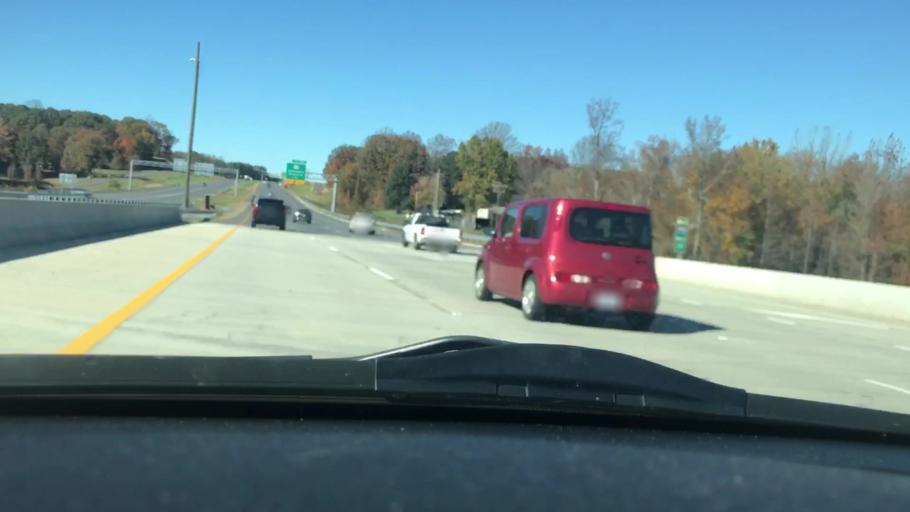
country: US
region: North Carolina
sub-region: Guilford County
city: Summerfield
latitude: 36.2287
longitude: -79.9141
